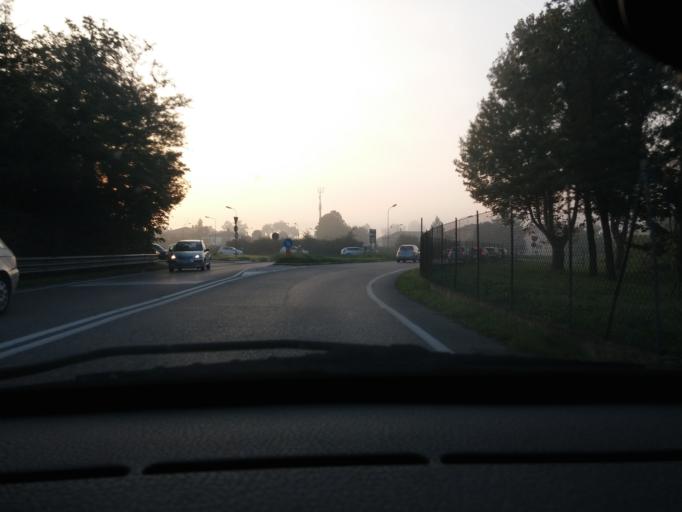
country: IT
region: Emilia-Romagna
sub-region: Provincia di Ferrara
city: Ferrara
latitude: 44.8354
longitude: 11.6004
